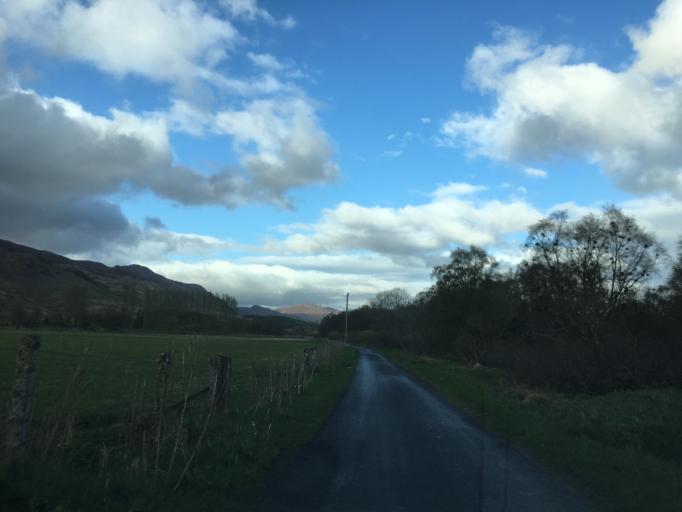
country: GB
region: Scotland
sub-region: Highland
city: Kingussie
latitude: 57.0130
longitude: -4.3274
